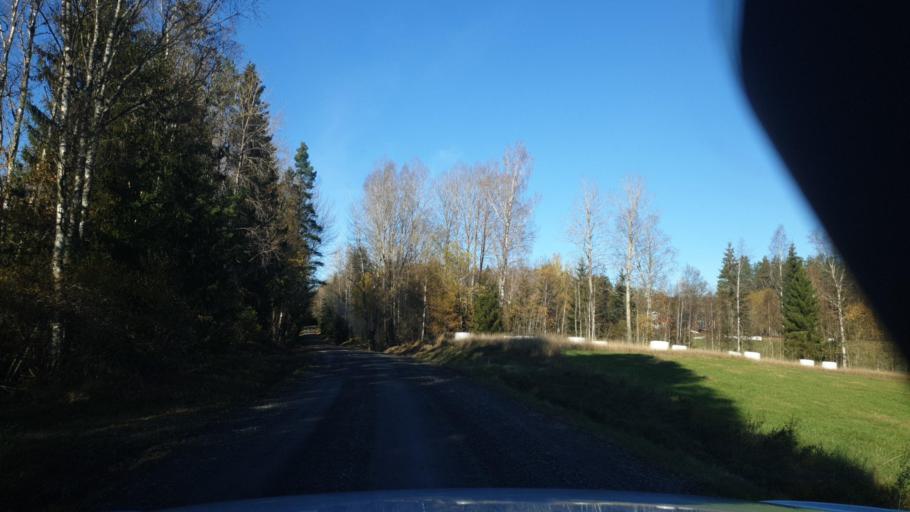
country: SE
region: Vaermland
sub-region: Karlstads Kommun
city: Edsvalla
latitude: 59.5123
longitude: 13.0172
